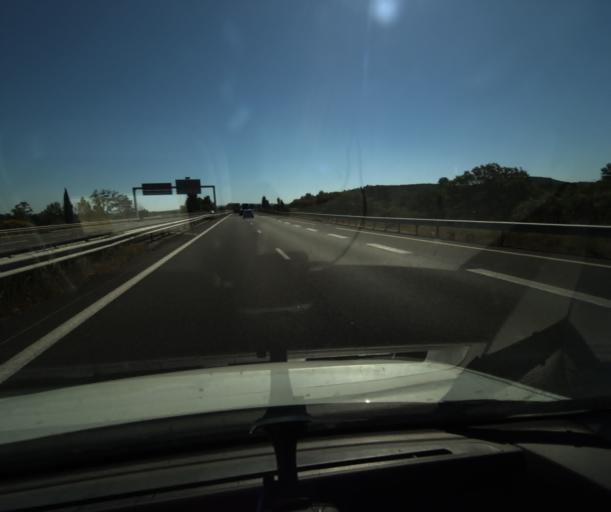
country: FR
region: Languedoc-Roussillon
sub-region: Departement de l'Aude
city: Ferrals-les-Corbieres
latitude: 43.1695
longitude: 2.7458
